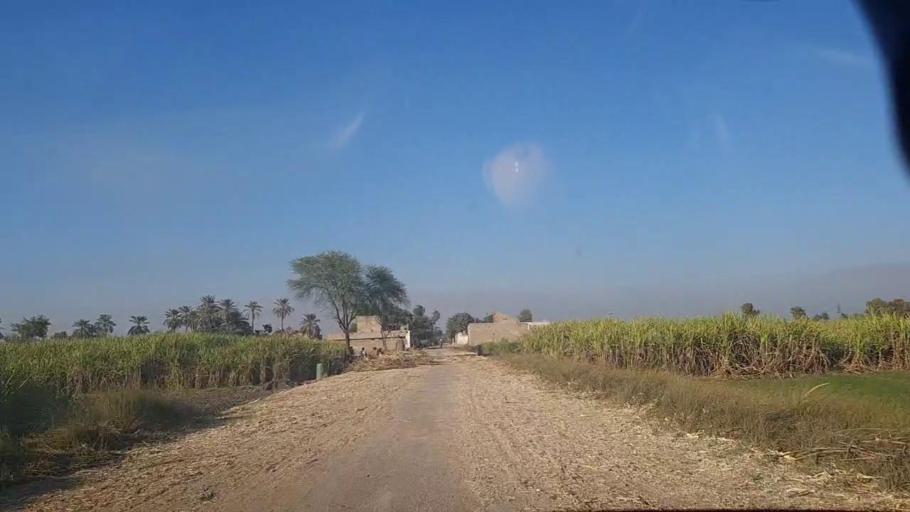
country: PK
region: Sindh
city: Sobhadero
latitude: 27.4162
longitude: 68.4230
